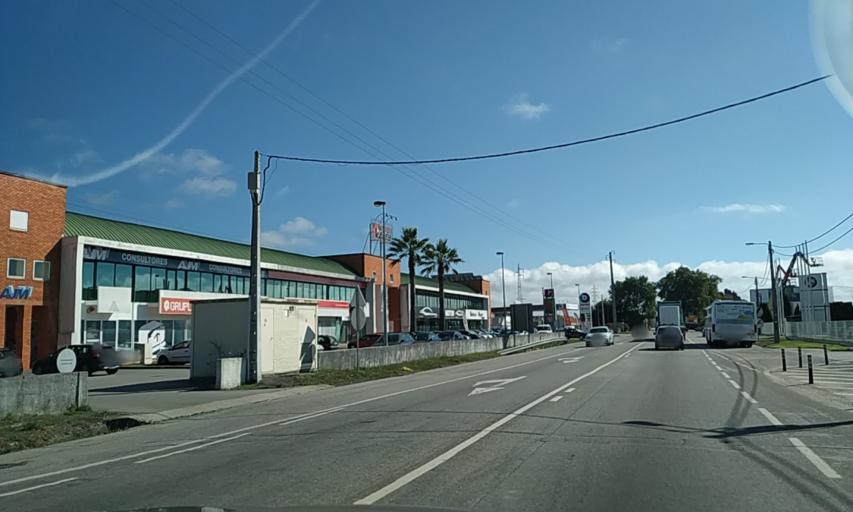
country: PT
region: Aveiro
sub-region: Aveiro
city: Aveiro
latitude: 40.6627
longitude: -8.6122
